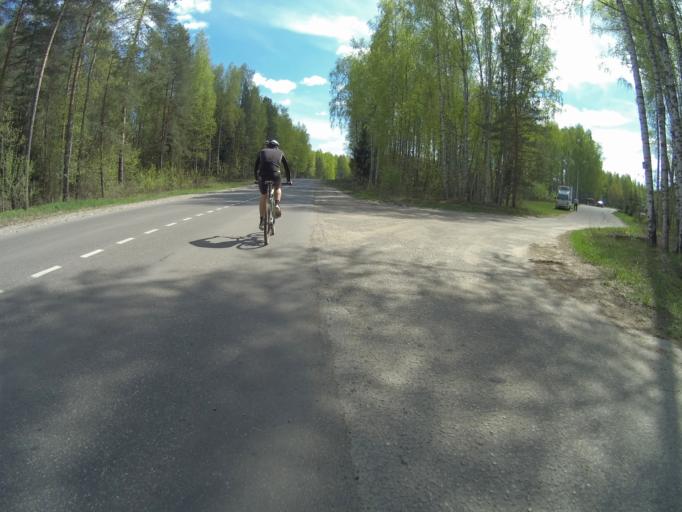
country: RU
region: Vladimir
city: Raduzhnyy
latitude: 55.9958
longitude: 40.2714
